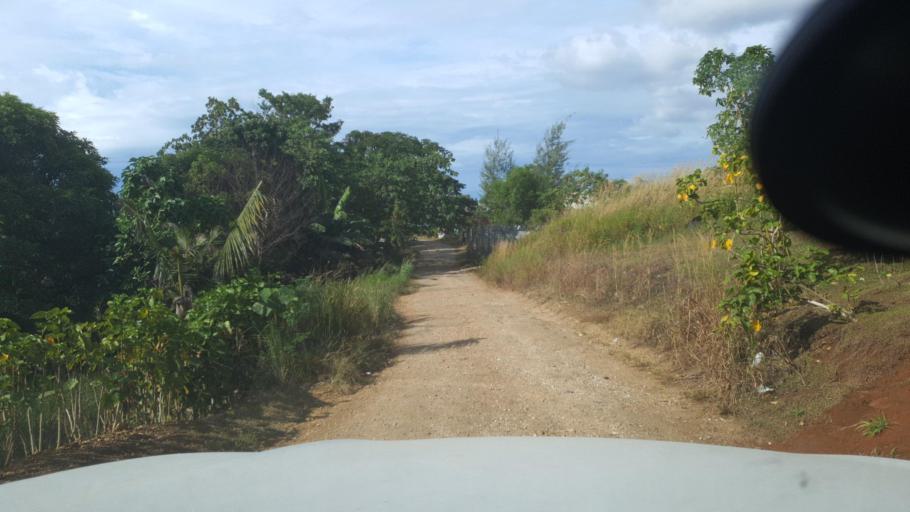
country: SB
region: Guadalcanal
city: Honiara
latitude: -9.4448
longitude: 159.9361
